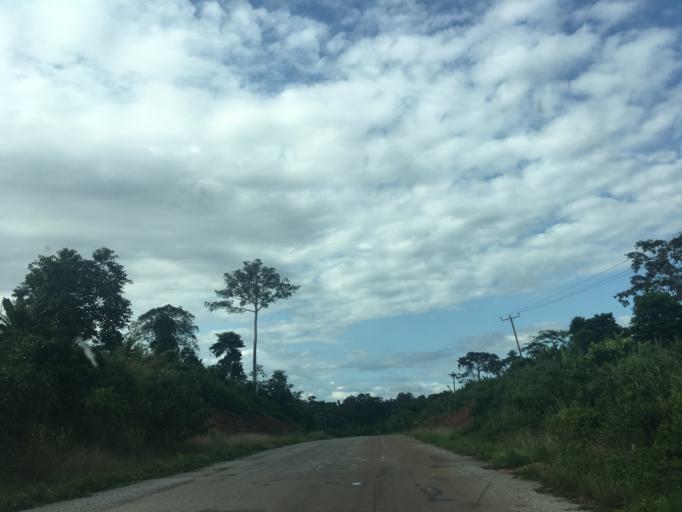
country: GH
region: Western
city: Wassa-Akropong
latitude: 6.0103
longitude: -2.4052
